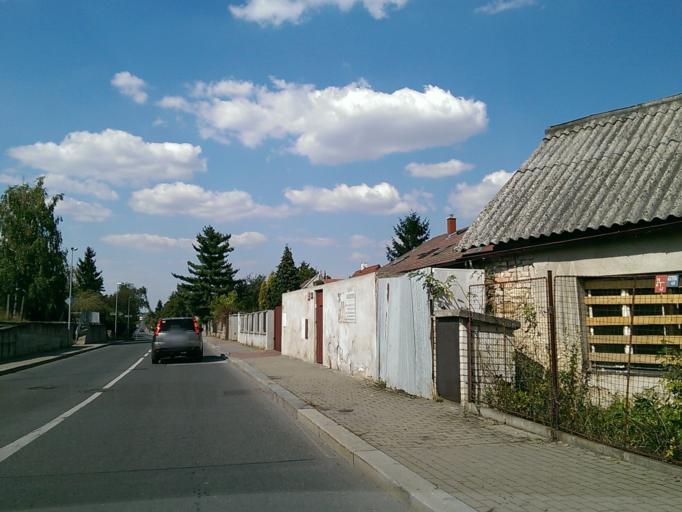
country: CZ
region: Praha
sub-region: Praha 14
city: Hostavice
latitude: 50.0725
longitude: 14.5550
